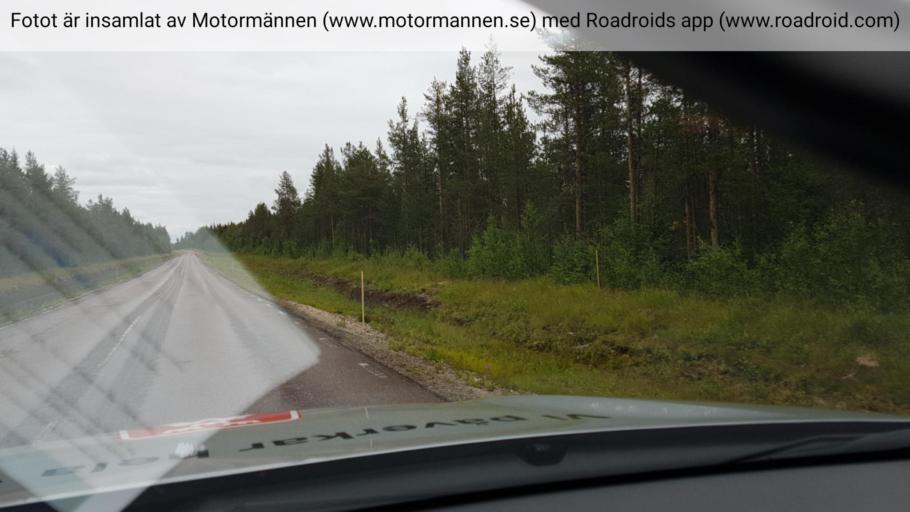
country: SE
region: Norrbotten
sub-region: Overkalix Kommun
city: OEverkalix
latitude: 67.0559
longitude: 22.3091
